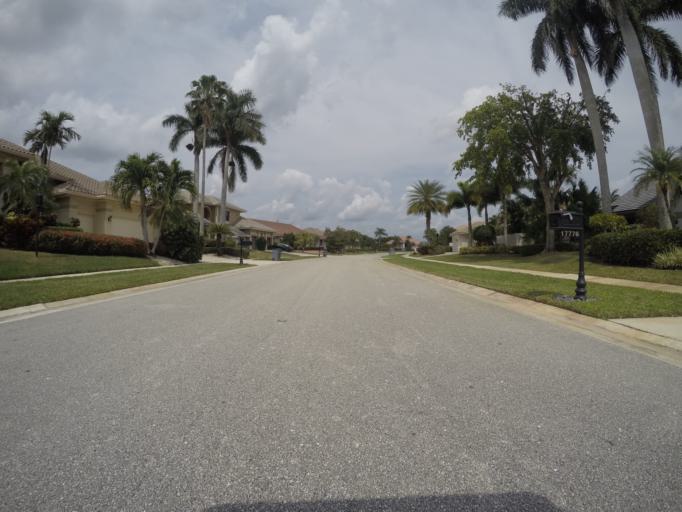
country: US
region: Florida
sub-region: Palm Beach County
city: Villages of Oriole
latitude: 26.4125
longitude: -80.2187
